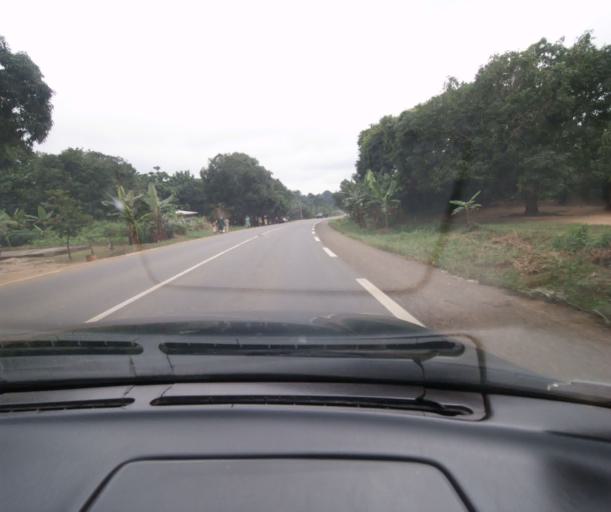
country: CM
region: Centre
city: Saa
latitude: 4.3389
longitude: 11.2833
